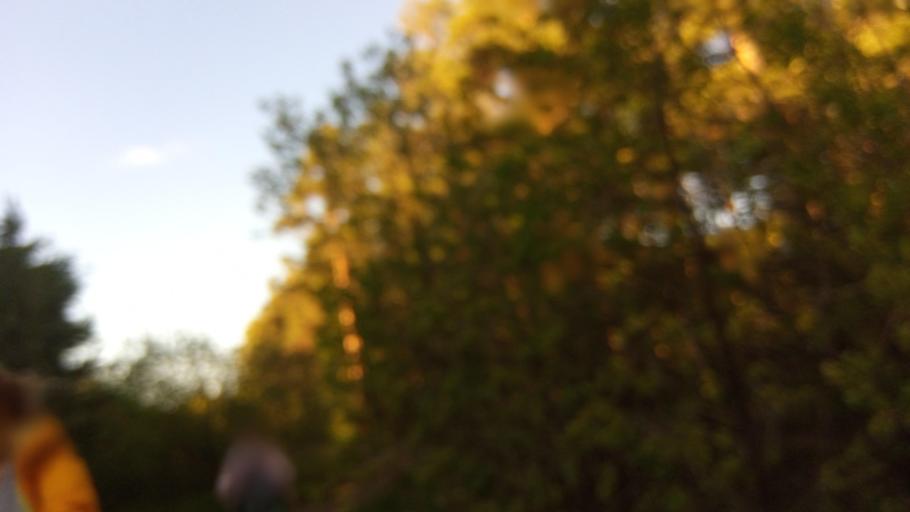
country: RU
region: Chelyabinsk
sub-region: Gorod Chelyabinsk
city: Chelyabinsk
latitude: 55.1378
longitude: 61.3291
